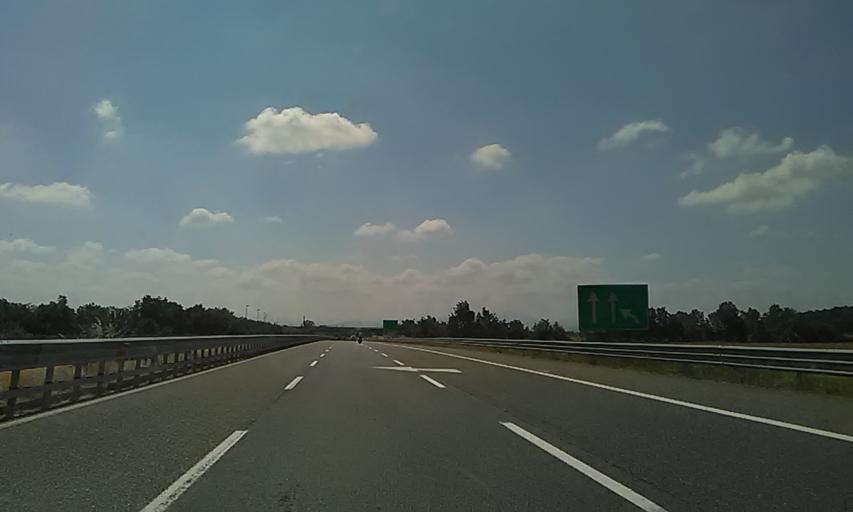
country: IT
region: Piedmont
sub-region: Provincia di Alessandria
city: Predosa
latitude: 44.7639
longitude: 8.6376
